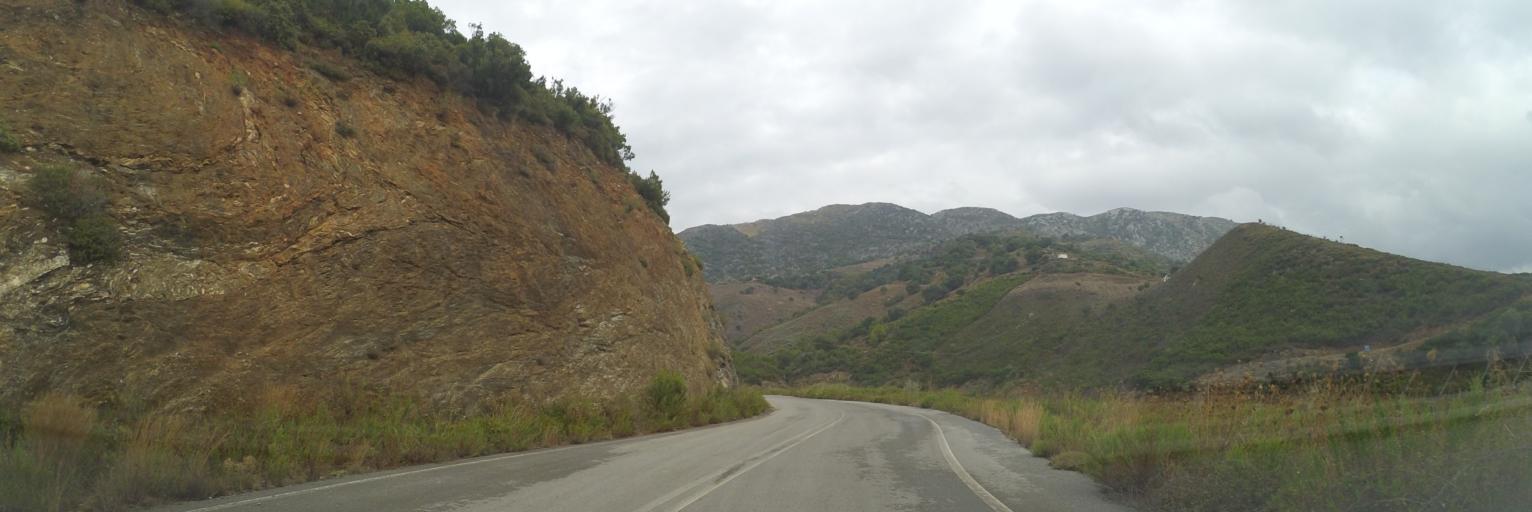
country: GR
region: Crete
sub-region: Nomos Rethymnis
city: Agia Foteini
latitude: 35.2841
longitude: 24.5728
